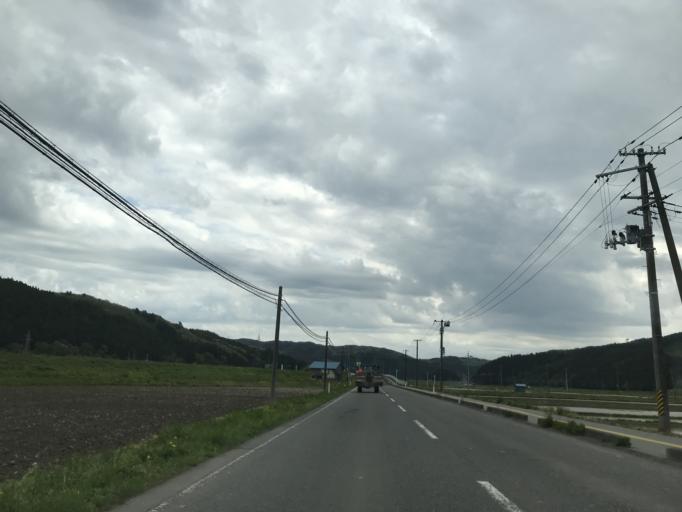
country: JP
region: Iwate
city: Ichinoseki
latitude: 38.7640
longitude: 141.3270
